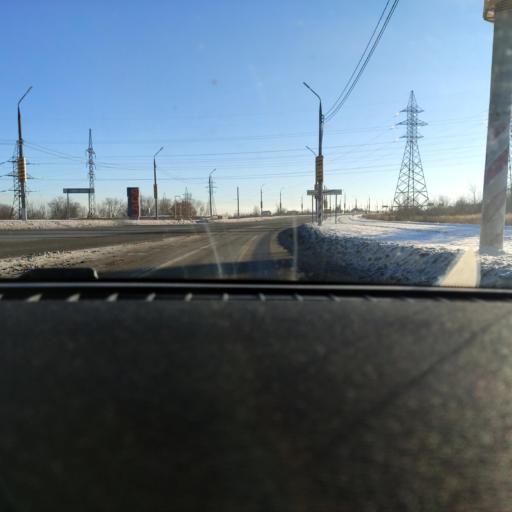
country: RU
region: Samara
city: Novokuybyshevsk
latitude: 53.0855
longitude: 49.9982
